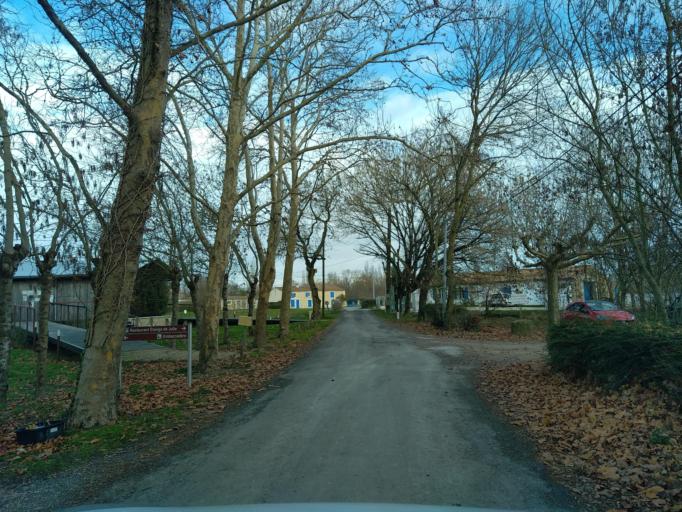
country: FR
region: Pays de la Loire
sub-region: Departement de la Vendee
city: Maillezais
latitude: 46.3179
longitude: -0.7757
